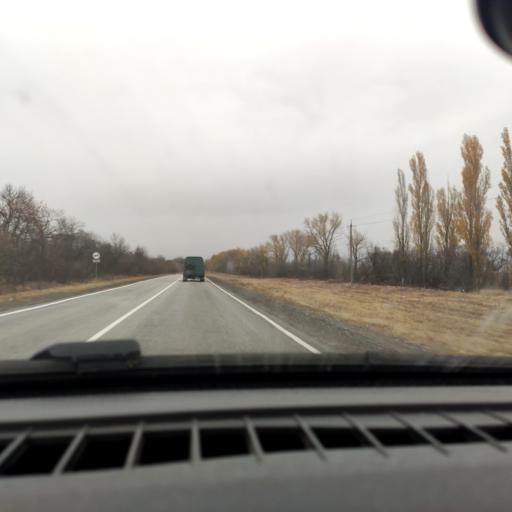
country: RU
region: Voronezj
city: Uryv-Pokrovka
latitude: 51.0781
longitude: 38.9971
